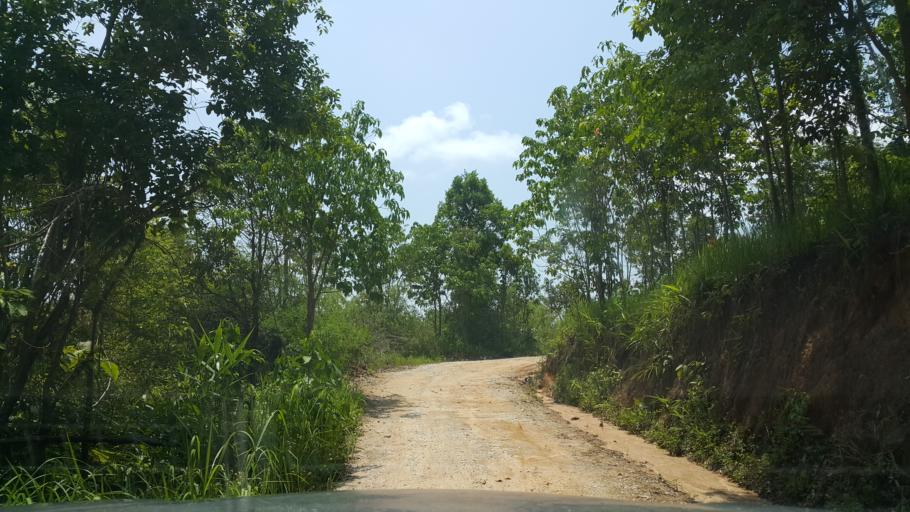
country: TH
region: Chiang Rai
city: Chiang Rai
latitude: 20.0001
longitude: 99.7187
